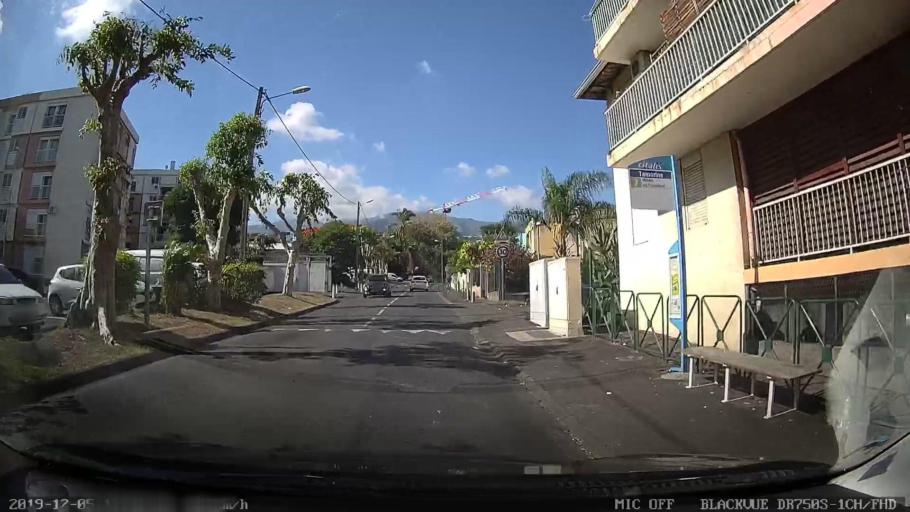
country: RE
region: Reunion
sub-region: Reunion
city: Saint-Denis
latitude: -20.8977
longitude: 55.4805
